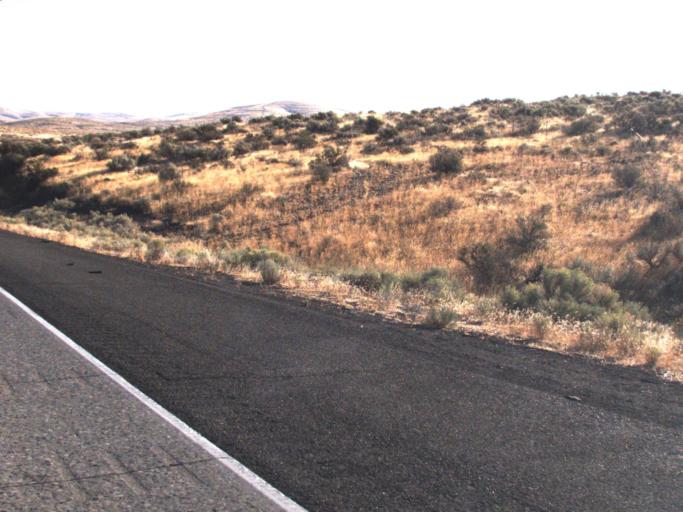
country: US
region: Washington
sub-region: Yakima County
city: Terrace Heights
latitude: 46.7891
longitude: -120.3620
